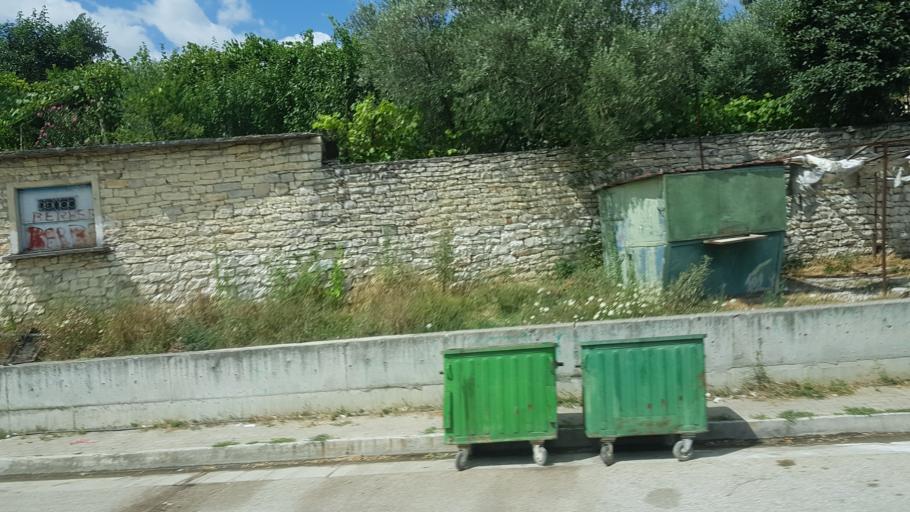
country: AL
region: Gjirokaster
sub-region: Rrethi i Tepelenes
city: Krahes
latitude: 40.4316
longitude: 19.8525
